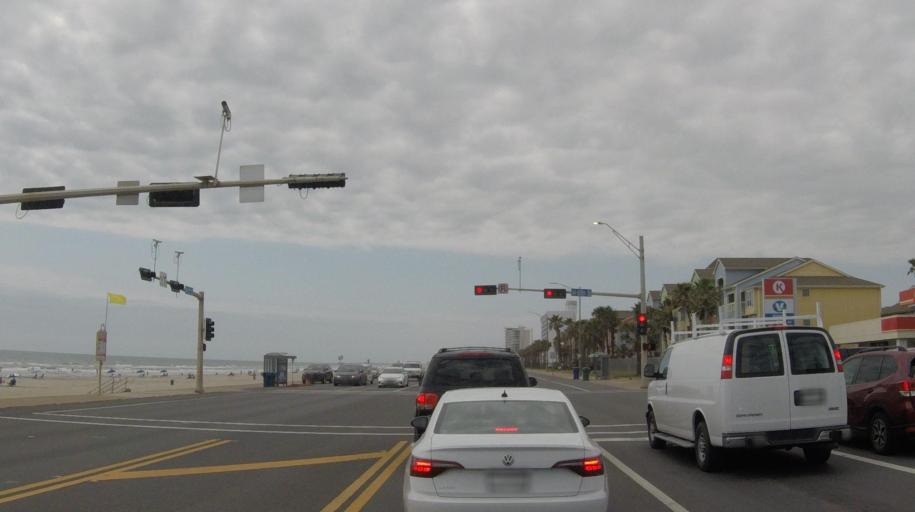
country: US
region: Texas
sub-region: Galveston County
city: Galveston
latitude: 29.2626
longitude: -94.8336
